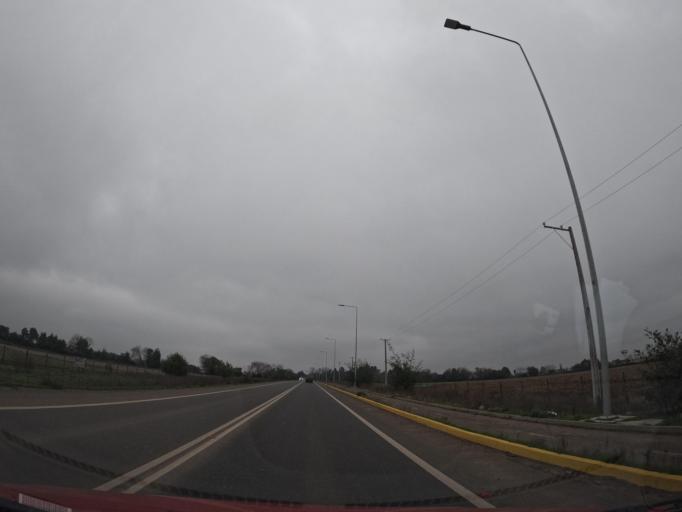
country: CL
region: Maule
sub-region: Provincia de Talca
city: San Clemente
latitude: -35.5400
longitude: -71.4733
